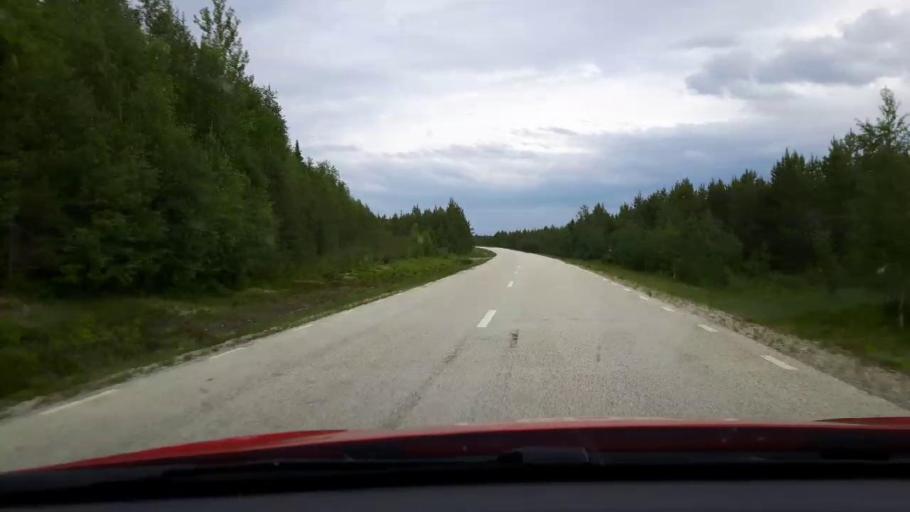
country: SE
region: Jaemtland
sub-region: Bergs Kommun
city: Hoverberg
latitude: 62.7084
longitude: 13.9353
